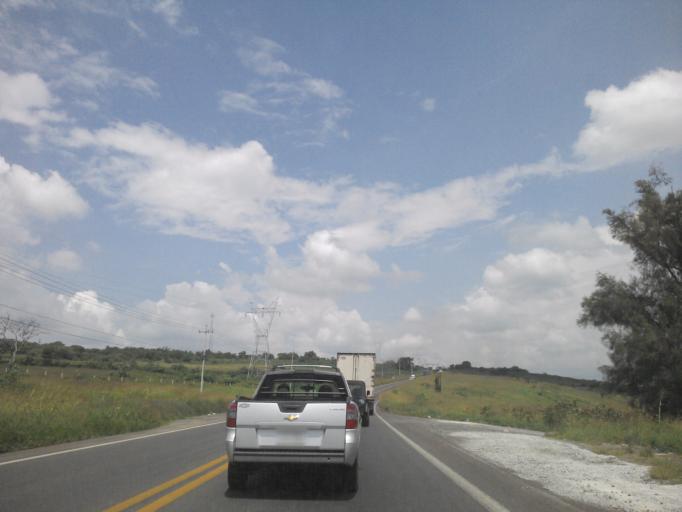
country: MX
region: Jalisco
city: Acatic
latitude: 20.6954
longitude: -102.9796
